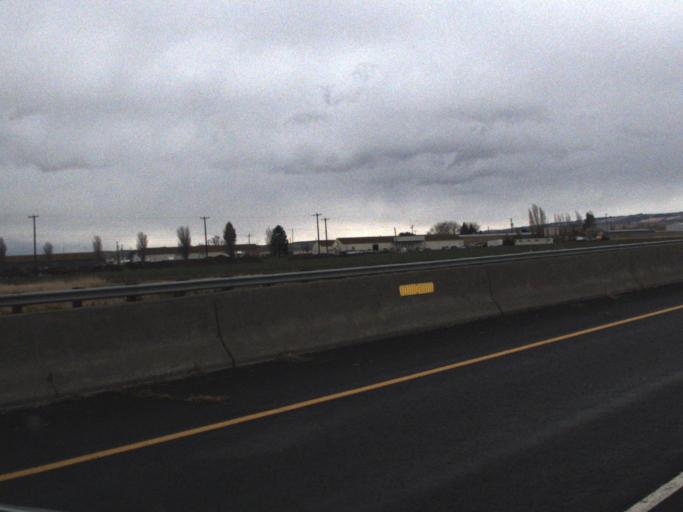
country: US
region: Washington
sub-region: Walla Walla County
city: Walla Walla East
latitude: 46.0840
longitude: -118.2814
